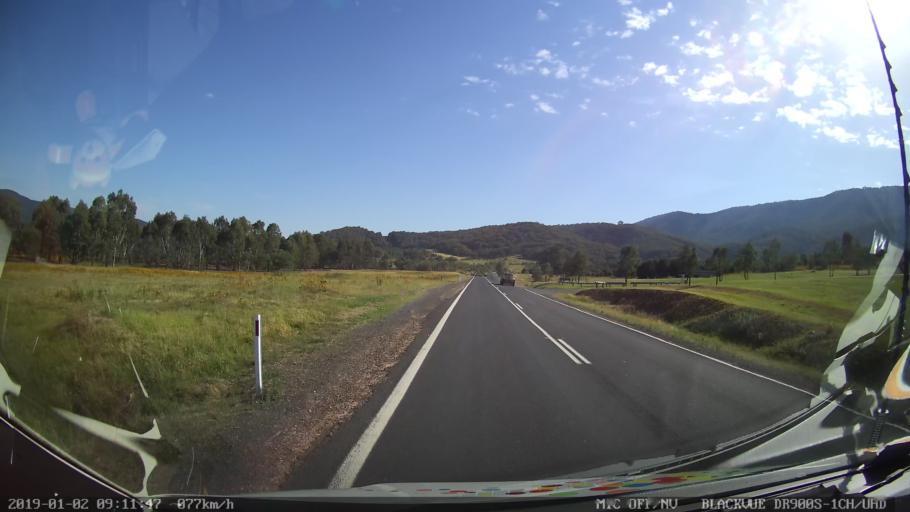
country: AU
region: New South Wales
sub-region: Tumut Shire
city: Tumut
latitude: -35.5081
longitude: 148.2706
